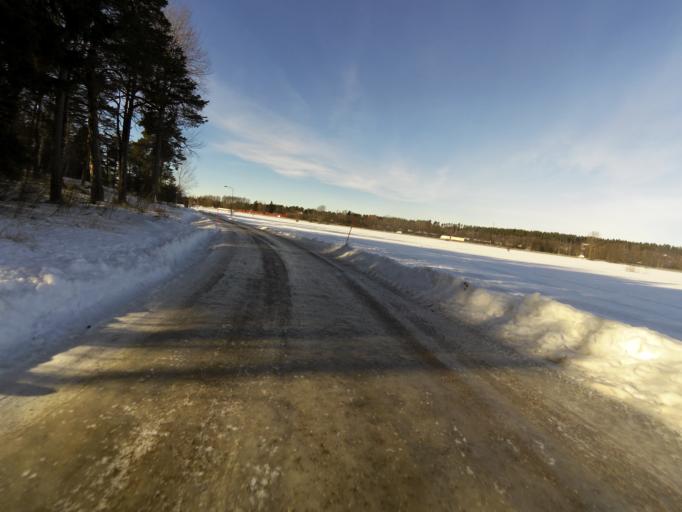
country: SE
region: Gaevleborg
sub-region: Gavle Kommun
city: Valbo
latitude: 60.6515
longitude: 17.0559
